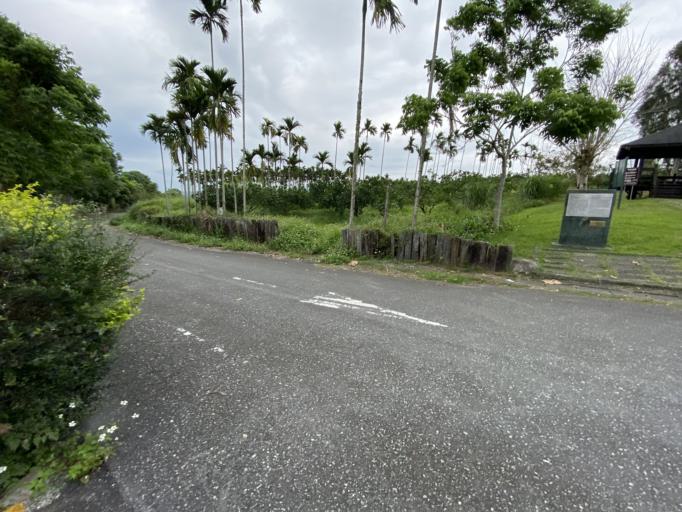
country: TW
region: Taiwan
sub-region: Hualien
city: Hualian
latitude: 23.4709
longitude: 121.3590
